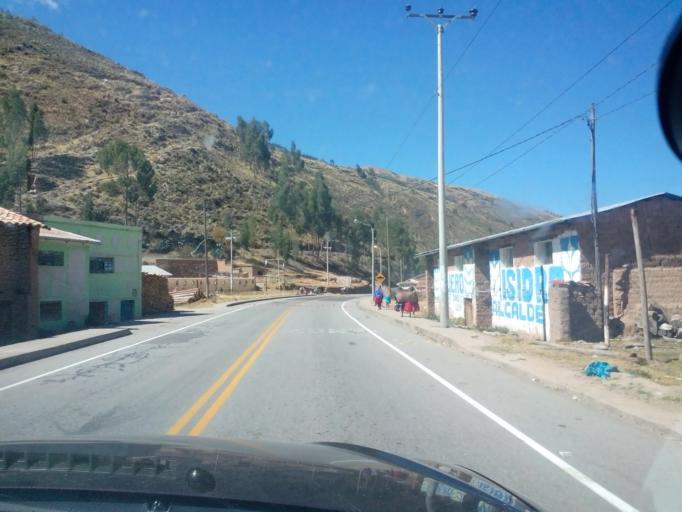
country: PE
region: Cusco
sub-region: Provincia de Canchis
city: Checacupe
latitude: -14.0296
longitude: -71.4538
